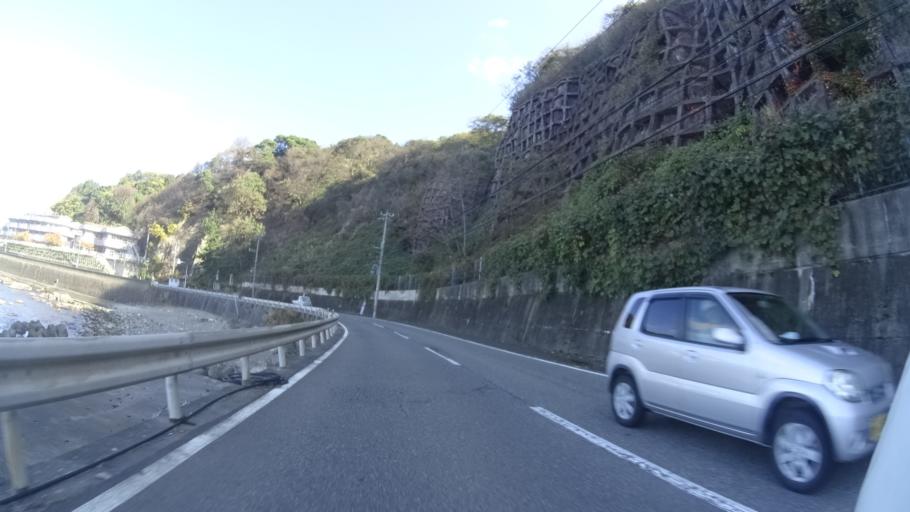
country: JP
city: Asahi
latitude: 35.8898
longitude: 135.9960
